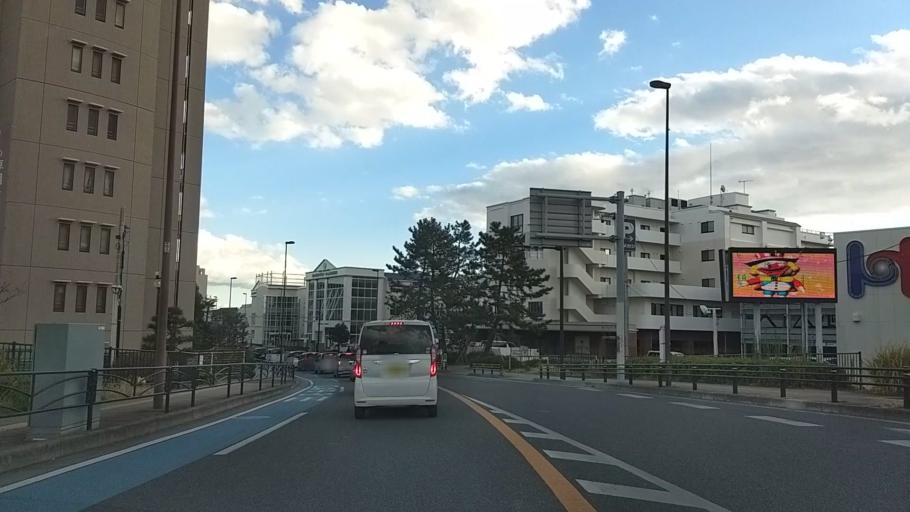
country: JP
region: Kanagawa
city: Chigasaki
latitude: 35.3295
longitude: 139.3901
